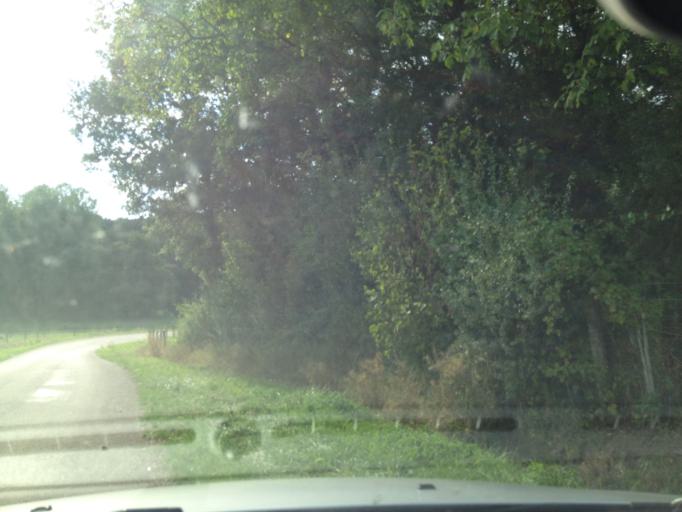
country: FR
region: Franche-Comte
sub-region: Departement de la Haute-Saone
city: Jussey
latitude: 47.8352
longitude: 5.9862
